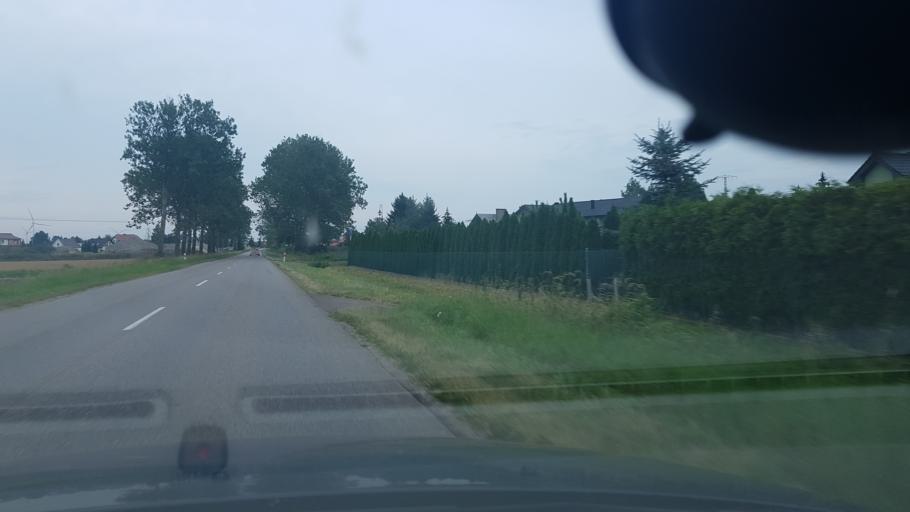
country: PL
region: Pomeranian Voivodeship
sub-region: Powiat nowodworski
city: Nowy Dwor Gdanski
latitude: 54.2173
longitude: 19.1089
